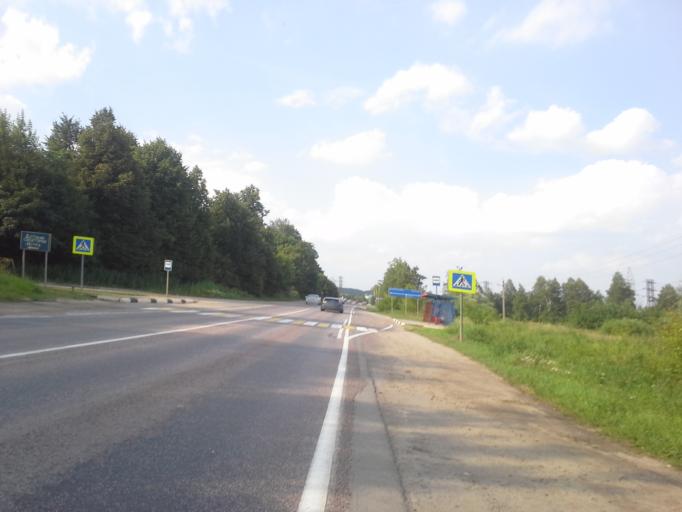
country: RU
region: Moskovskaya
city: Istra
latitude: 55.9036
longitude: 36.8080
